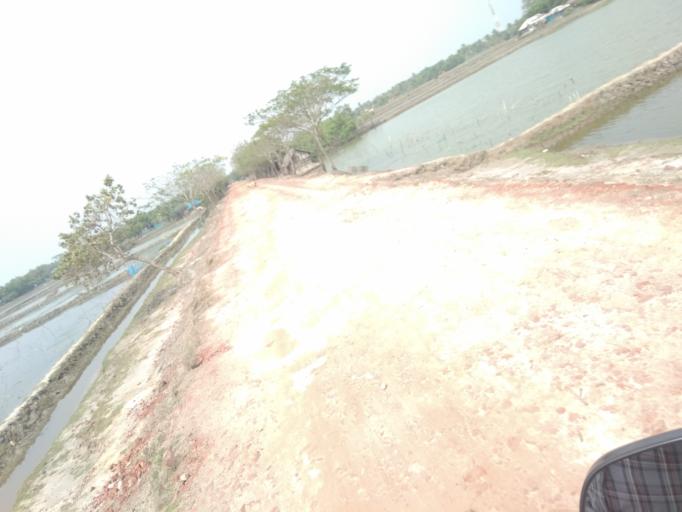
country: IN
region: West Bengal
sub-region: North 24 Parganas
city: Taki
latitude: 22.2945
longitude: 89.2704
